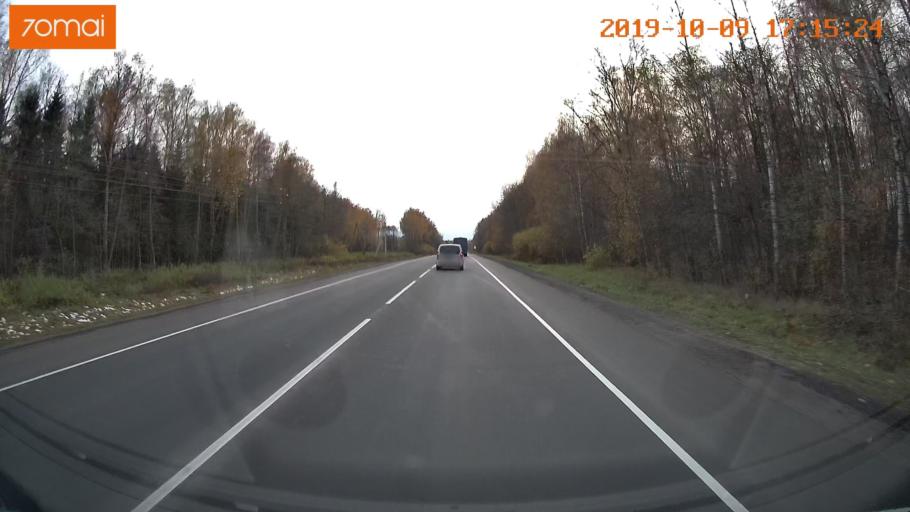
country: RU
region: Ivanovo
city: Furmanov
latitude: 57.2980
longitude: 41.1909
